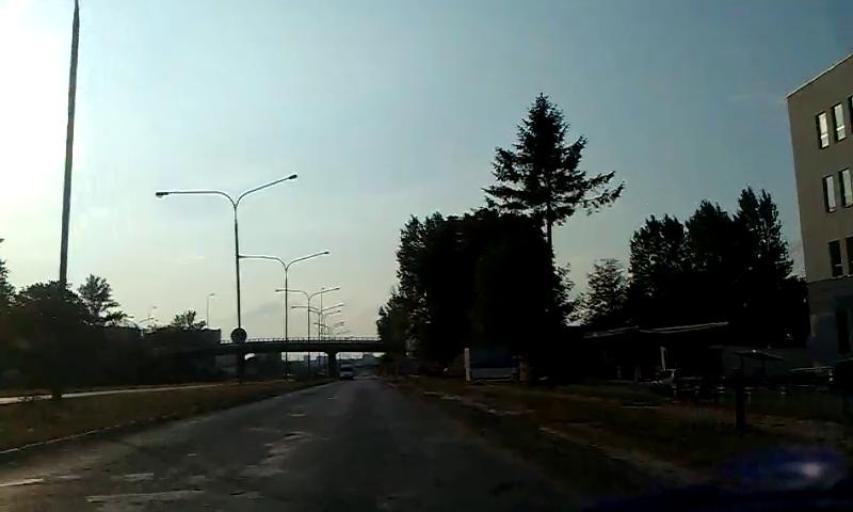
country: PL
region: Lublin Voivodeship
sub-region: Powiat lubelski
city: Lublin
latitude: 51.2335
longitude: 22.6050
